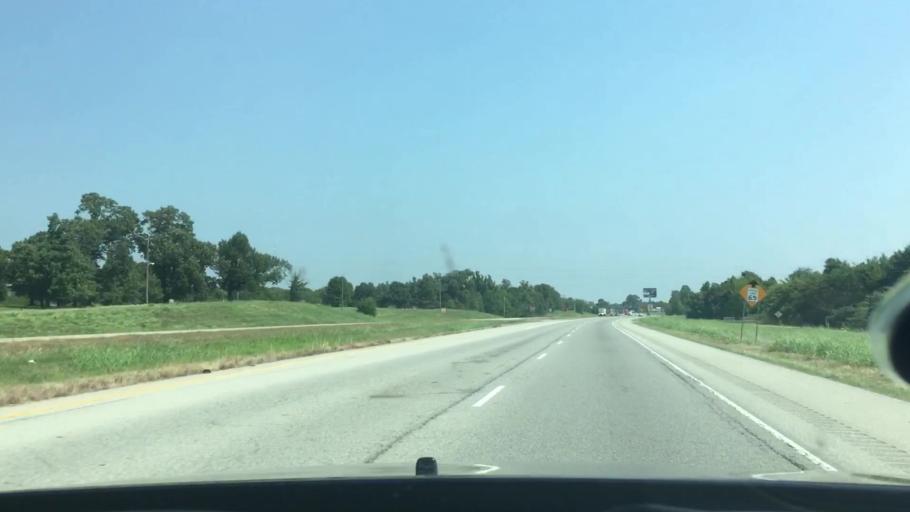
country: US
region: Oklahoma
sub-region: Atoka County
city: Atoka
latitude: 34.3088
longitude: -96.1758
